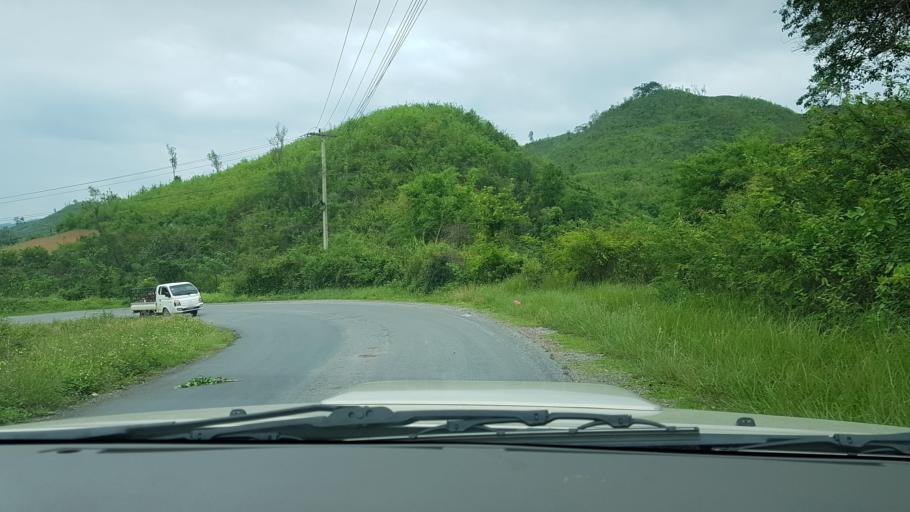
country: LA
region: Loungnamtha
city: Muang Nale
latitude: 20.3710
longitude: 101.7196
